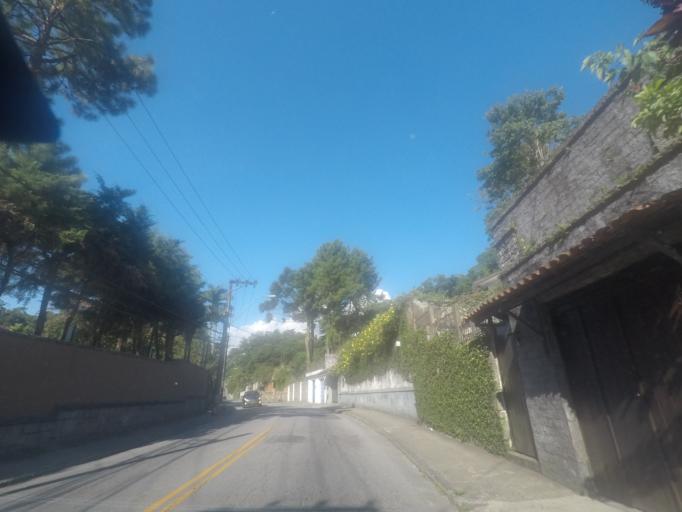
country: BR
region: Rio de Janeiro
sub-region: Petropolis
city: Petropolis
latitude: -22.5340
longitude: -43.1957
